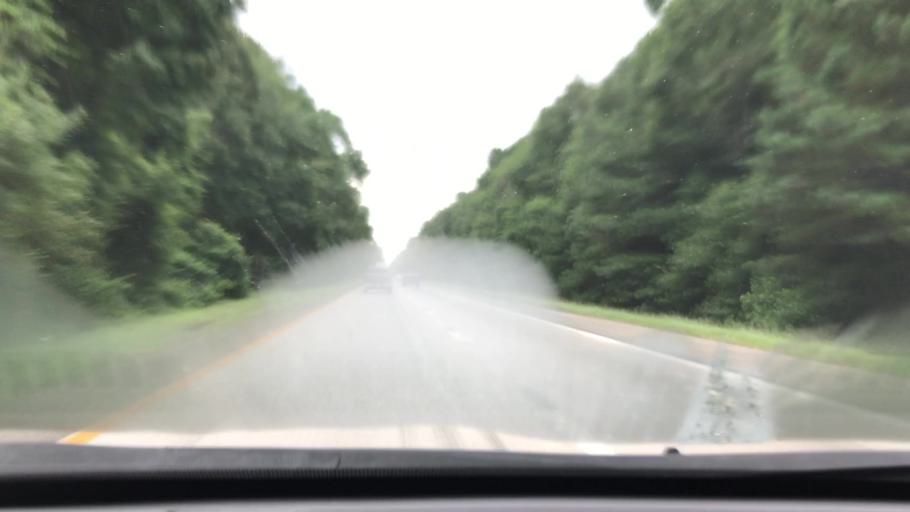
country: US
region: South Carolina
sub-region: Jasper County
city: Ridgeland
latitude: 32.4034
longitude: -81.0179
